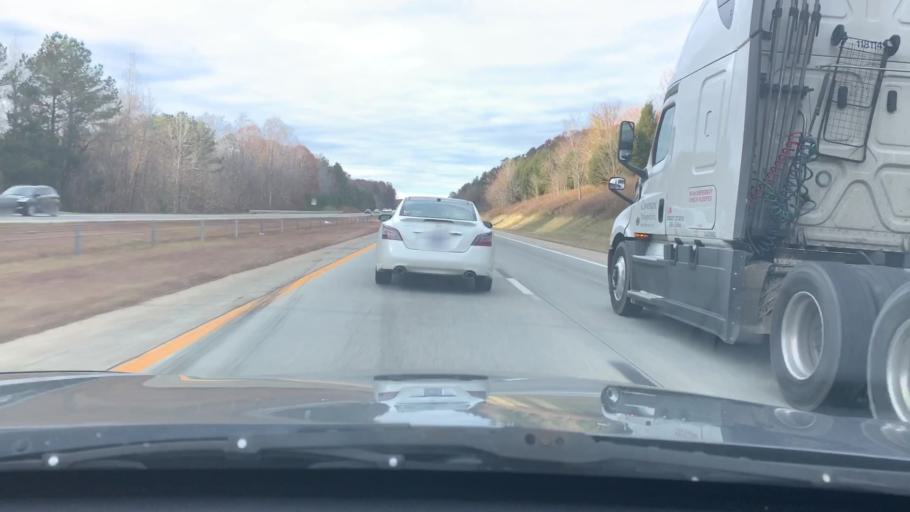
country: US
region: North Carolina
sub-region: Orange County
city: Hillsborough
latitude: 35.9991
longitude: -79.0775
